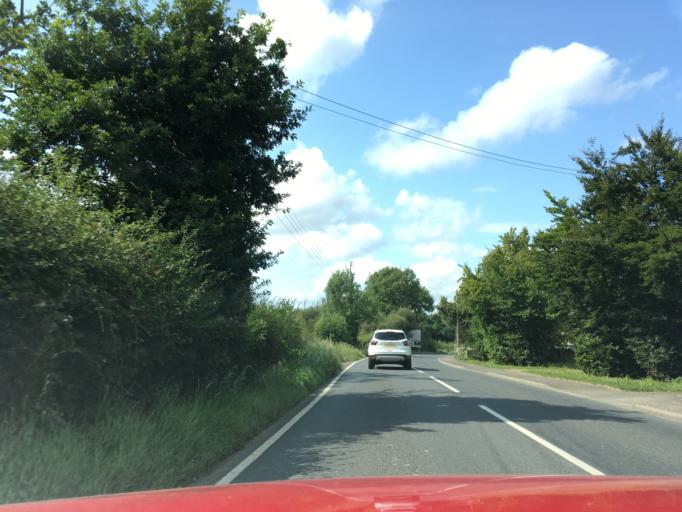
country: GB
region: England
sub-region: Kent
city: Headcorn
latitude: 51.1252
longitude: 0.6478
